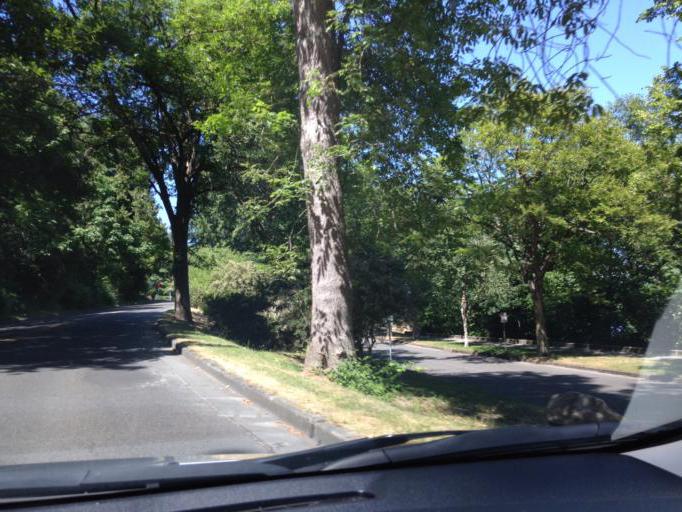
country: US
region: Washington
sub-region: King County
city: Seattle
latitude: 47.5845
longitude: -122.2879
